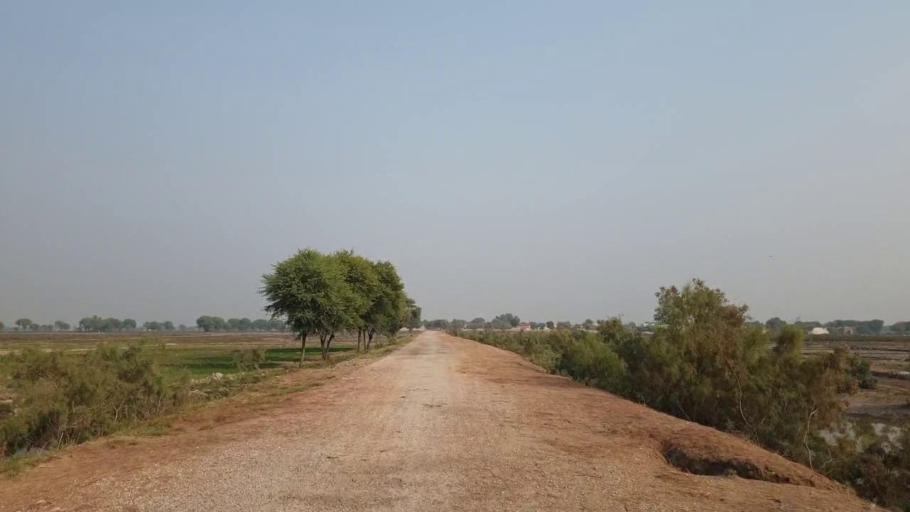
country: PK
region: Sindh
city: Bhan
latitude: 26.4584
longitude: 67.7240
